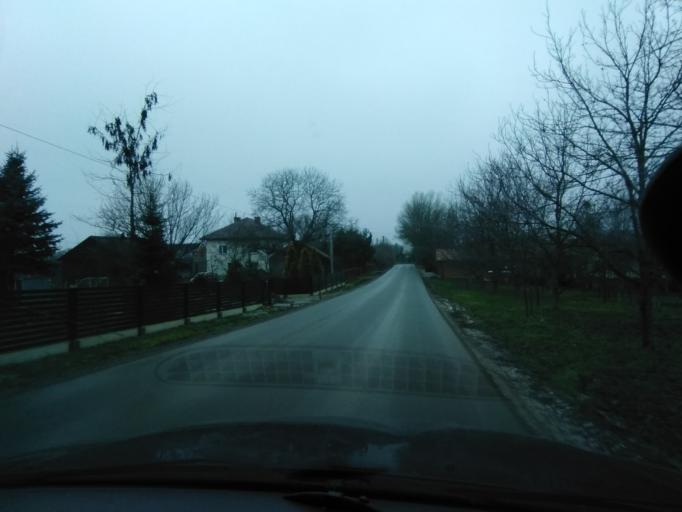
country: PL
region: Subcarpathian Voivodeship
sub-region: Powiat przeworski
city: Zurawiczki
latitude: 50.0037
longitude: 22.4821
